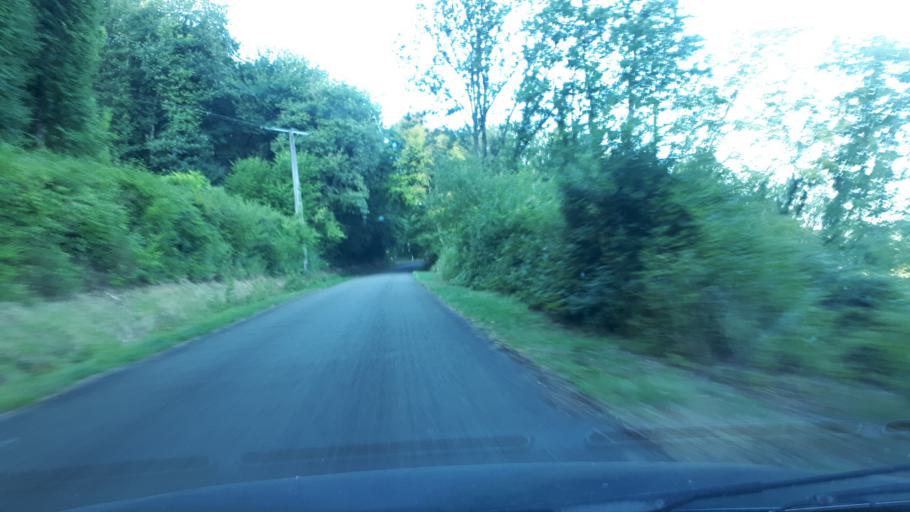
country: FR
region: Centre
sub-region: Departement du Loir-et-Cher
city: Villiers-sur-Loir
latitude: 47.7704
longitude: 0.9592
